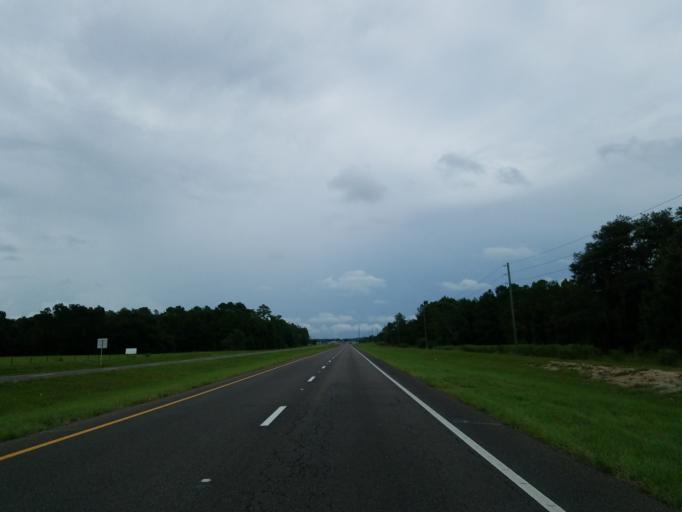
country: US
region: Florida
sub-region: Sumter County
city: Wildwood
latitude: 28.8784
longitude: -82.1142
